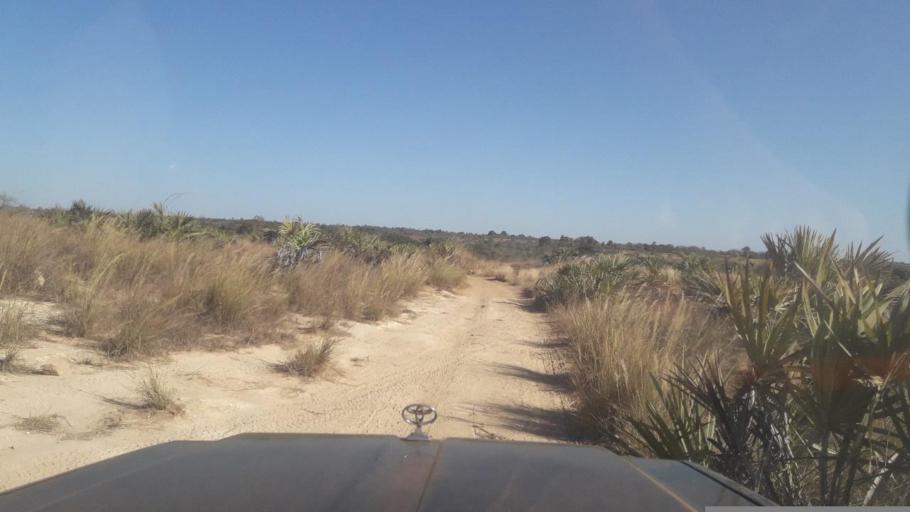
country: MG
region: Boeny
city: Sitampiky
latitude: -16.3868
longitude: 45.5905
